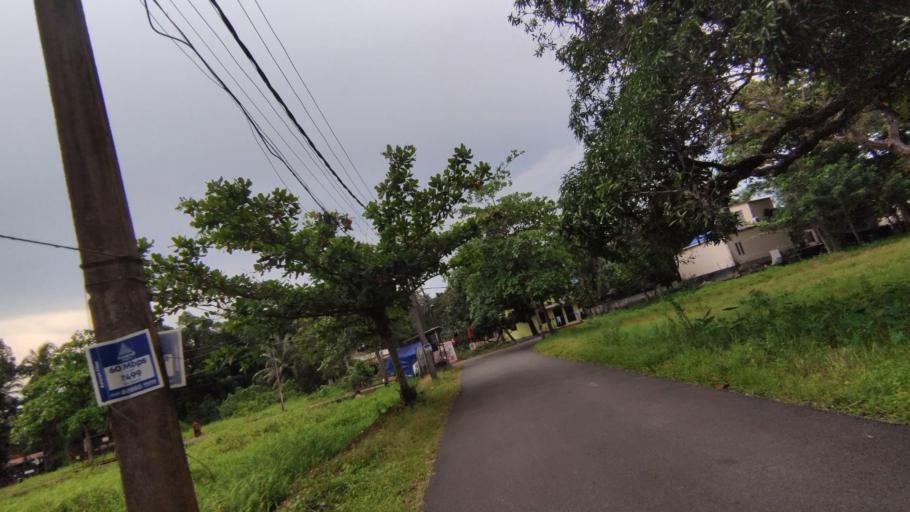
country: IN
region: Kerala
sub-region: Kottayam
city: Kottayam
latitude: 9.5731
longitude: 76.4920
